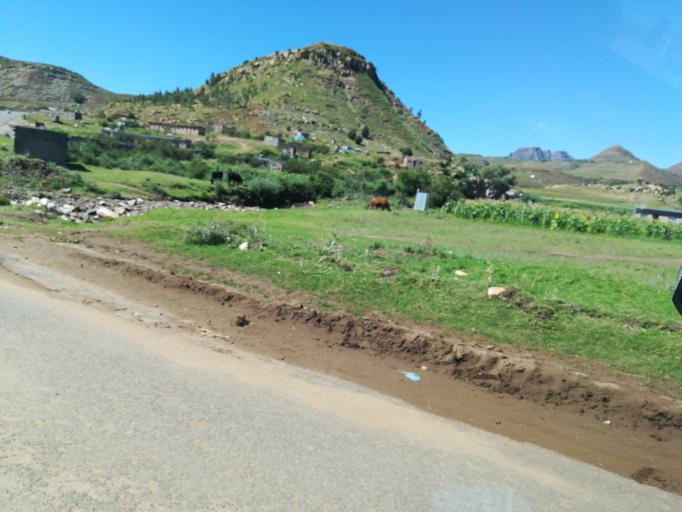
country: LS
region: Mohale's Hoek District
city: Mohale's Hoek
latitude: -30.0990
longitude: 27.4790
